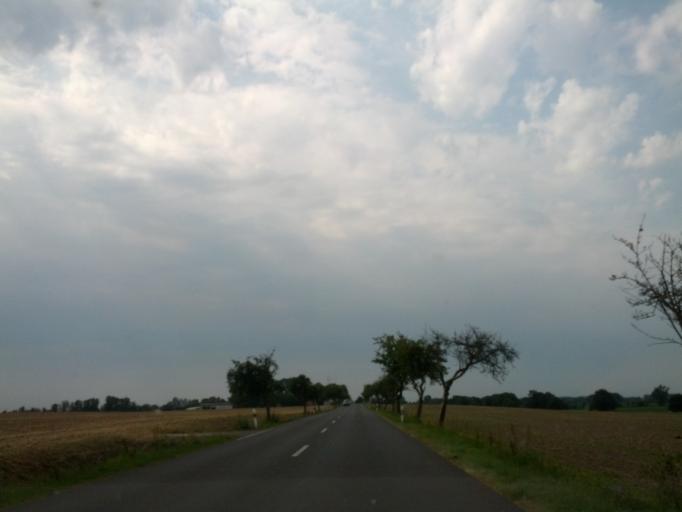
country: DE
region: Brandenburg
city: Kremmen
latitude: 52.7523
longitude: 12.8999
